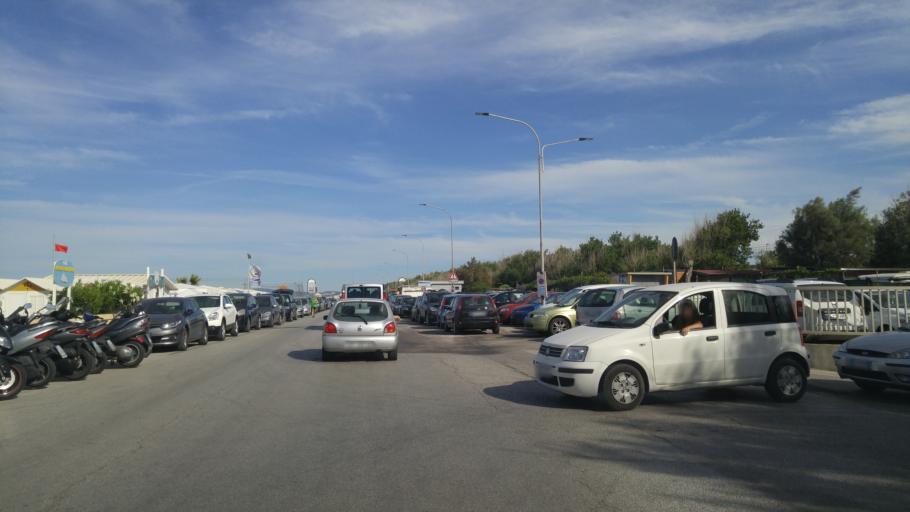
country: IT
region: The Marches
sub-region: Provincia di Ancona
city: Montignano-Marzocca
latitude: 43.6892
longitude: 13.2667
